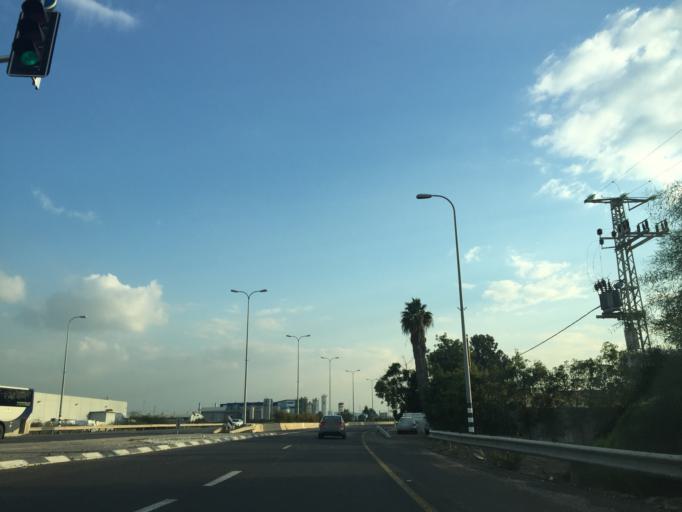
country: IL
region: Central District
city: Ramla
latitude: 31.9226
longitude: 34.8846
